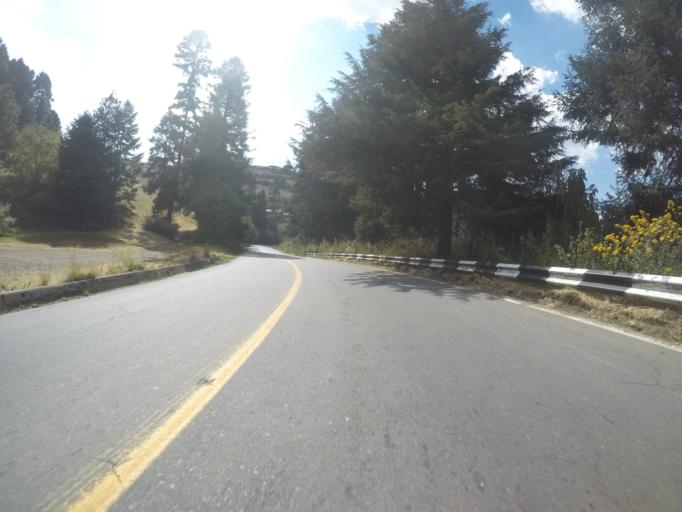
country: MX
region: Mexico
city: Cerro La Calera
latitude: 19.1763
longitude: -99.8029
